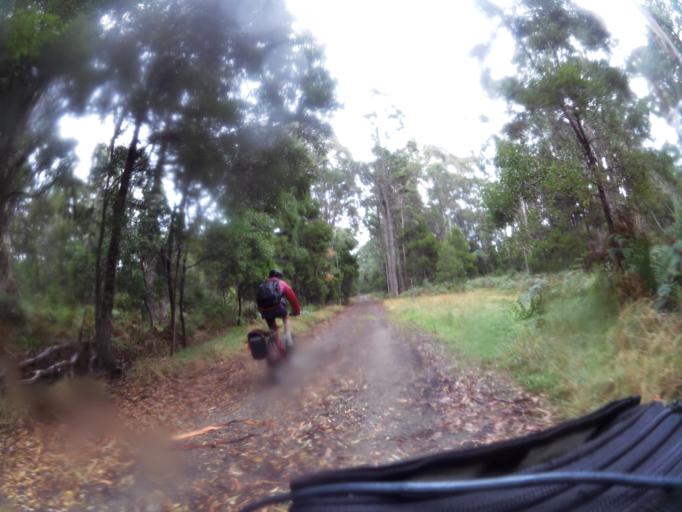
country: AU
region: New South Wales
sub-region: Greater Hume Shire
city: Holbrook
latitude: -36.1915
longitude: 147.5409
